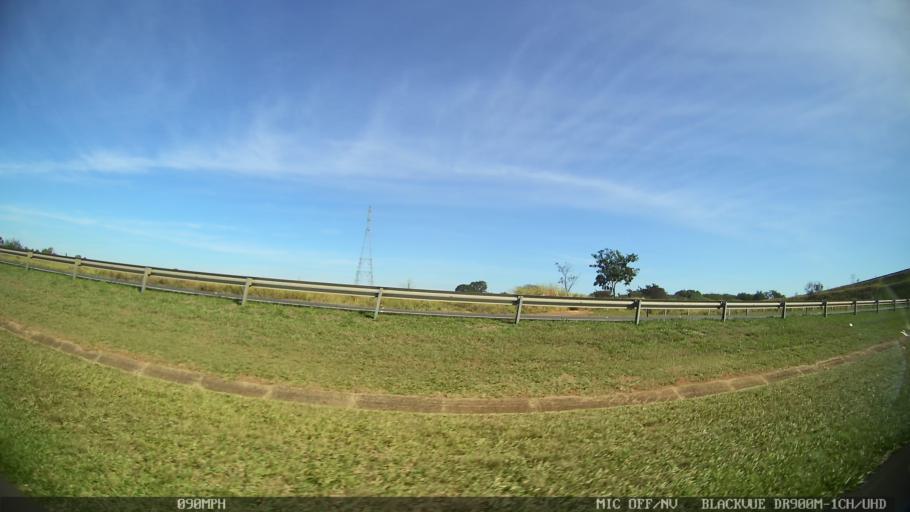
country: BR
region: Sao Paulo
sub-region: Pirassununga
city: Pirassununga
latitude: -21.9312
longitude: -47.4686
